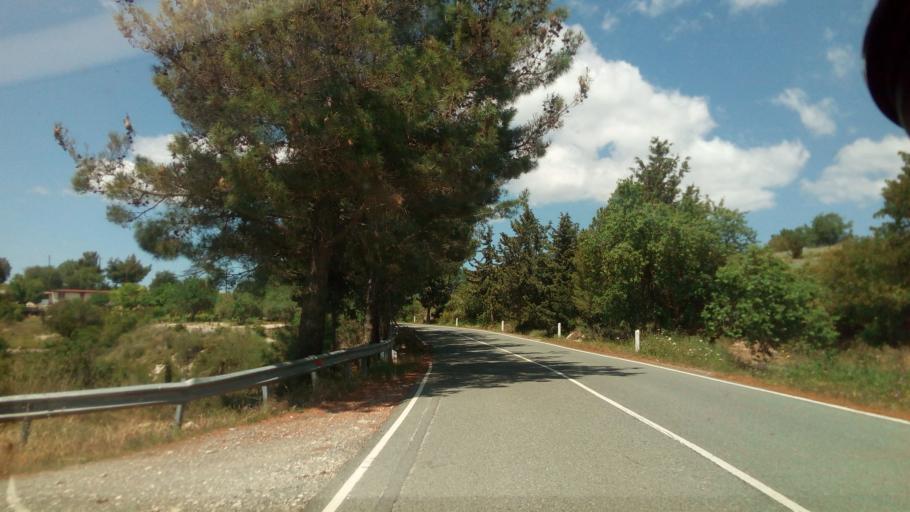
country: CY
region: Limassol
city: Pachna
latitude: 34.8359
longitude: 32.7721
